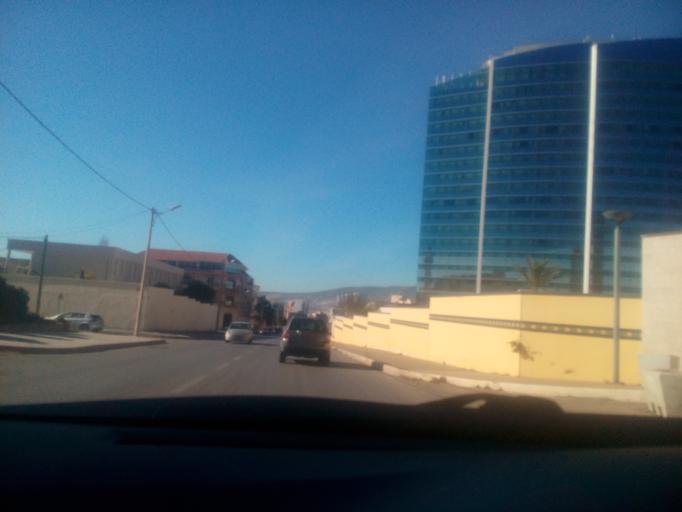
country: DZ
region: Oran
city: Oran
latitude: 35.7154
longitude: -0.6077
